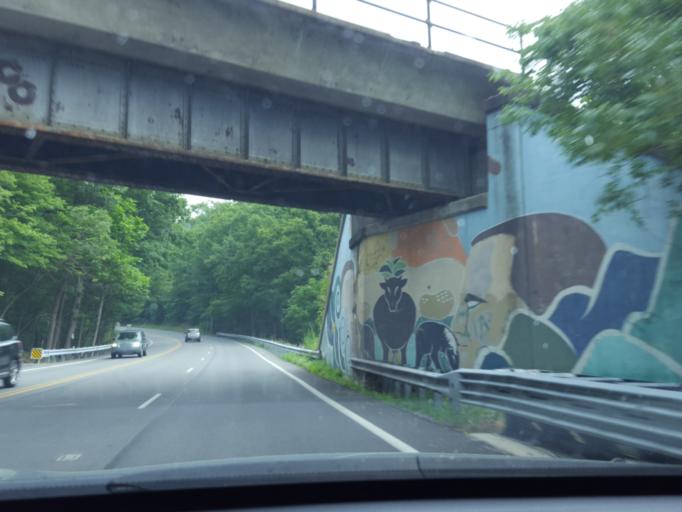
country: US
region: Virginia
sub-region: City of Waynesboro
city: Waynesboro
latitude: 38.0461
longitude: -78.8642
